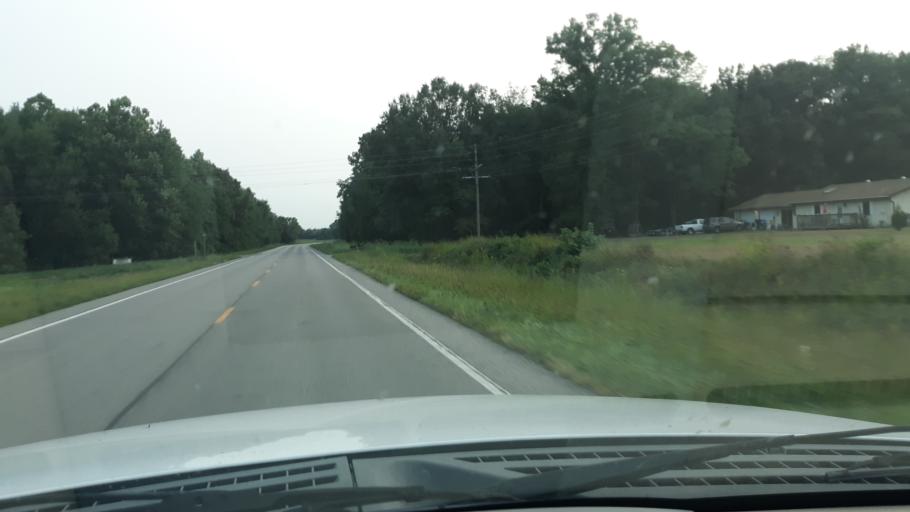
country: US
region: Illinois
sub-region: White County
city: Norris City
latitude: 37.9746
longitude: -88.3196
